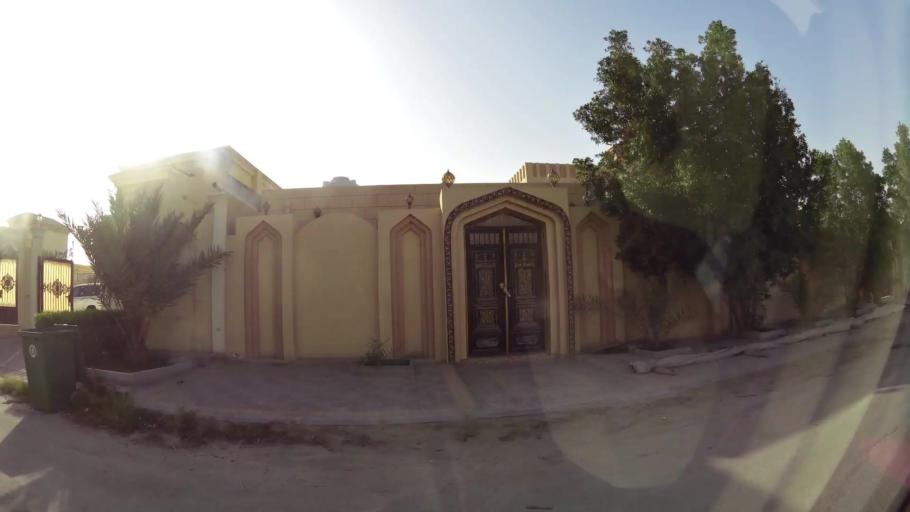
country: QA
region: Baladiyat ar Rayyan
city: Ar Rayyan
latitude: 25.3368
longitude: 51.4321
